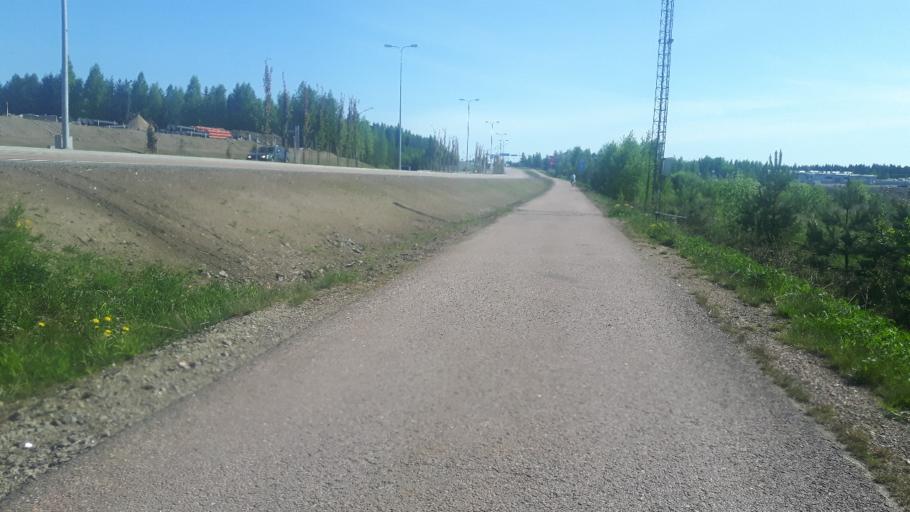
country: FI
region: Kymenlaakso
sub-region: Kotka-Hamina
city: Virojoki
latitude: 60.6005
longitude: 27.8305
